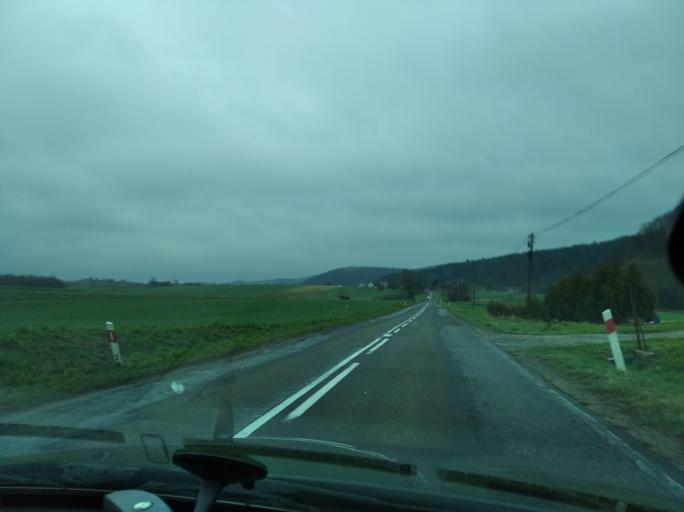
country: PL
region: Subcarpathian Voivodeship
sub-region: Powiat rzeszowski
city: Dynow
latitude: 49.8512
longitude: 22.2469
